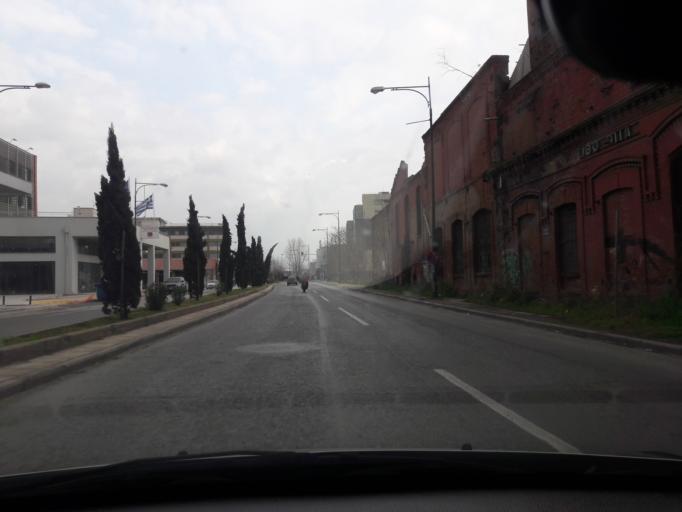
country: GR
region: Central Macedonia
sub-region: Nomos Thessalonikis
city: Thessaloniki
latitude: 40.6414
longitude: 22.9166
